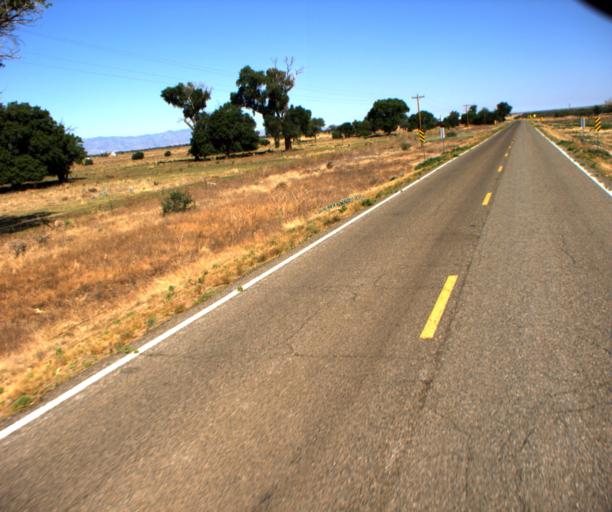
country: US
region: Arizona
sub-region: Graham County
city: Swift Trail Junction
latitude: 32.5870
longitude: -109.9649
